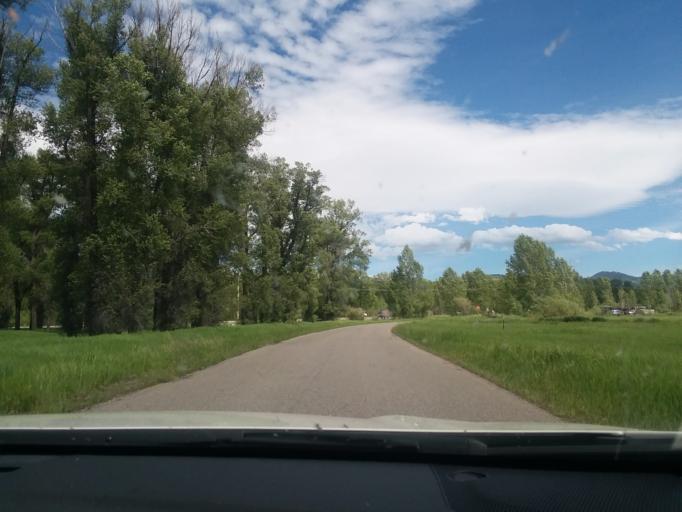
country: US
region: Wyoming
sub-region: Teton County
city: Moose Wilson Road
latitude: 43.5032
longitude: -110.8482
